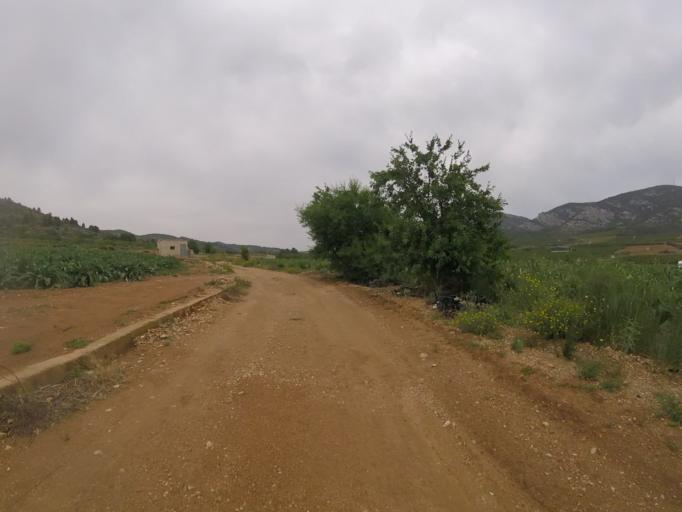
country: ES
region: Valencia
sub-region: Provincia de Castello
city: Alcala de Xivert
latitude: 40.2825
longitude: 0.2561
